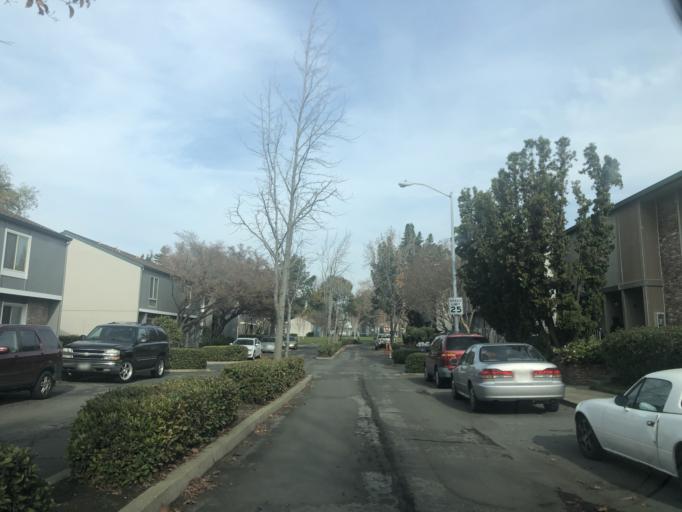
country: US
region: California
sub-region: Contra Costa County
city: Concord
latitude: 38.0012
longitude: -122.0397
